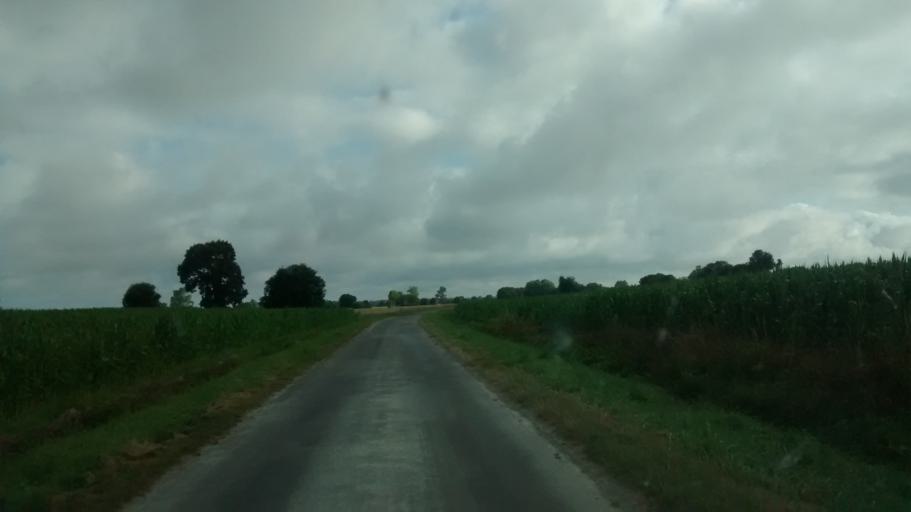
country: FR
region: Brittany
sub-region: Departement d'Ille-et-Vilaine
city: La Gouesniere
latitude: 48.6005
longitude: -1.8774
